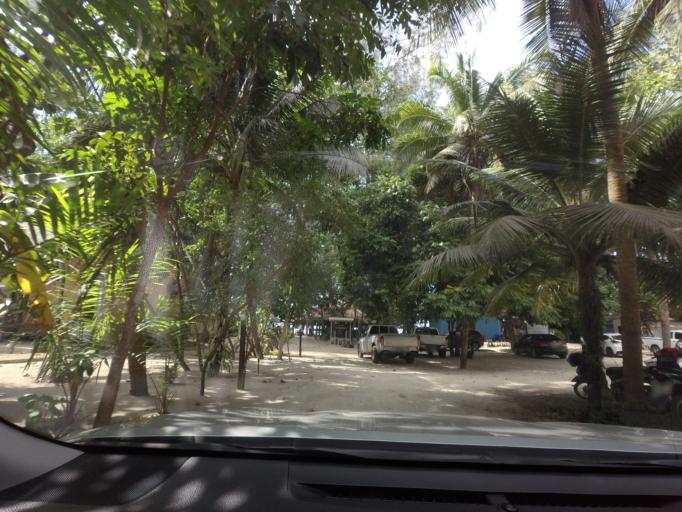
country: TH
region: Phangnga
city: Ban Khao Lak
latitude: 8.7379
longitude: 98.2429
